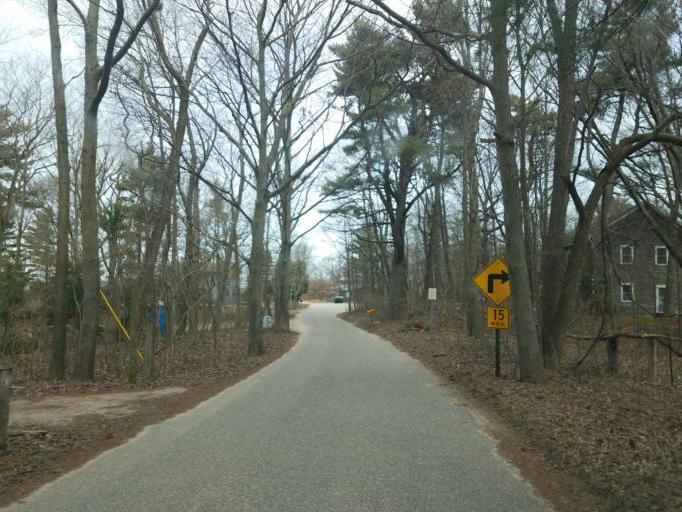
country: US
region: Michigan
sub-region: Oceana County
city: Hart
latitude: 43.6549
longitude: -86.5380
